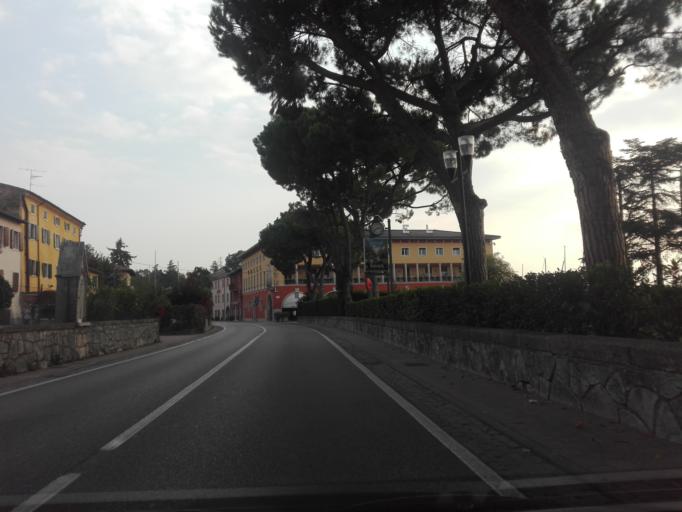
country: IT
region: Veneto
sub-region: Provincia di Verona
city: Bardolino
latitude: 45.5310
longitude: 10.7264
